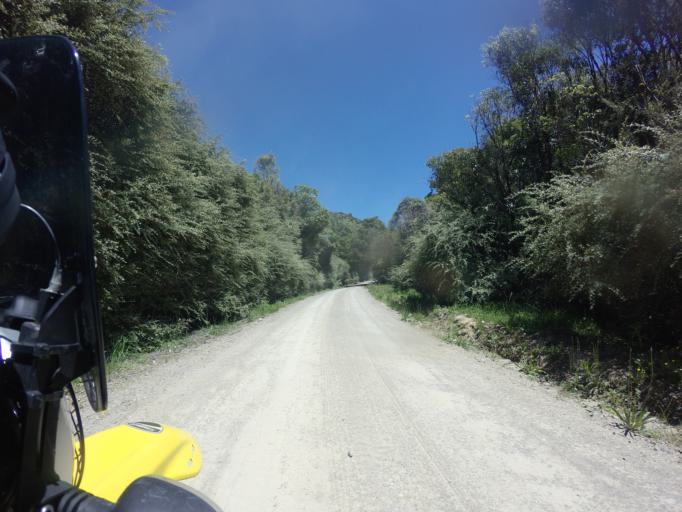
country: NZ
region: Bay of Plenty
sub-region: Opotiki District
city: Opotiki
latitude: -38.4088
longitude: 177.4271
